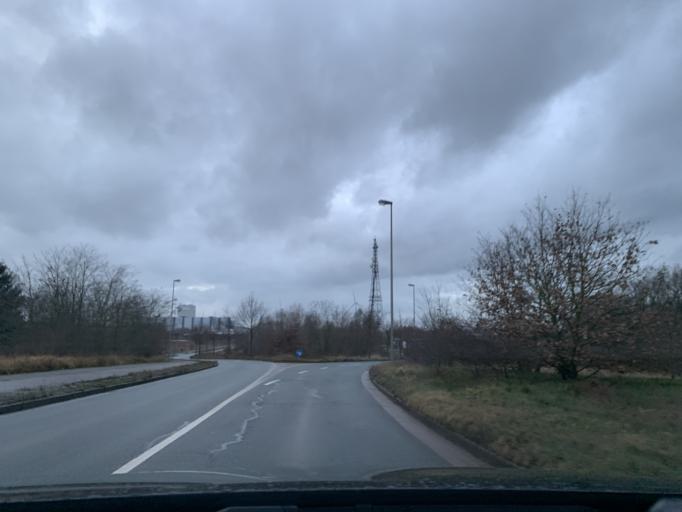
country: DE
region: Lower Saxony
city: Ritterhude
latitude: 53.1376
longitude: 8.7079
